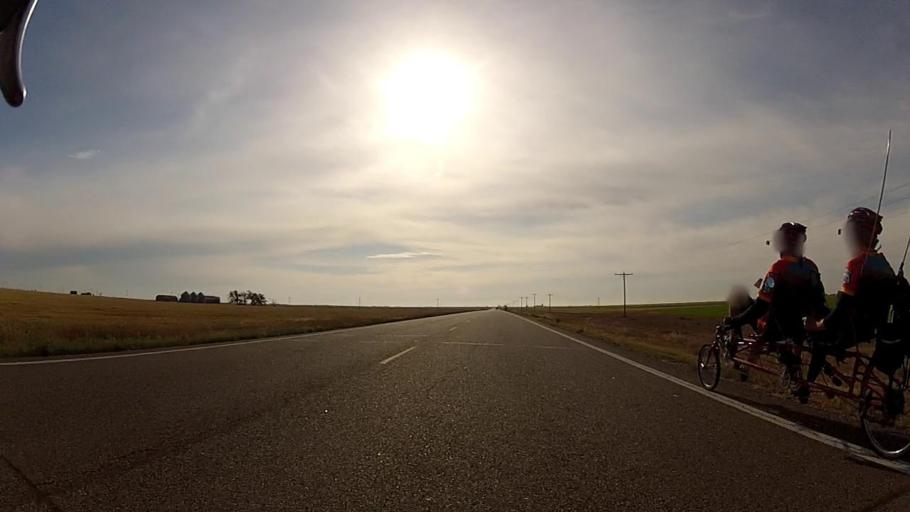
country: US
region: Kansas
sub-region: Grant County
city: Ulysses
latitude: 37.5766
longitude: -101.4744
